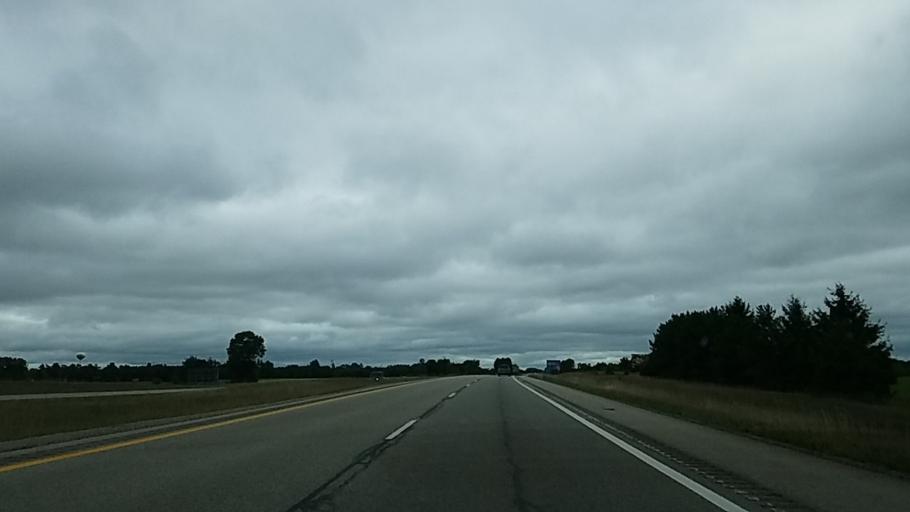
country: US
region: Michigan
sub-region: Otsego County
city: Gaylord
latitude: 45.0510
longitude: -84.6880
